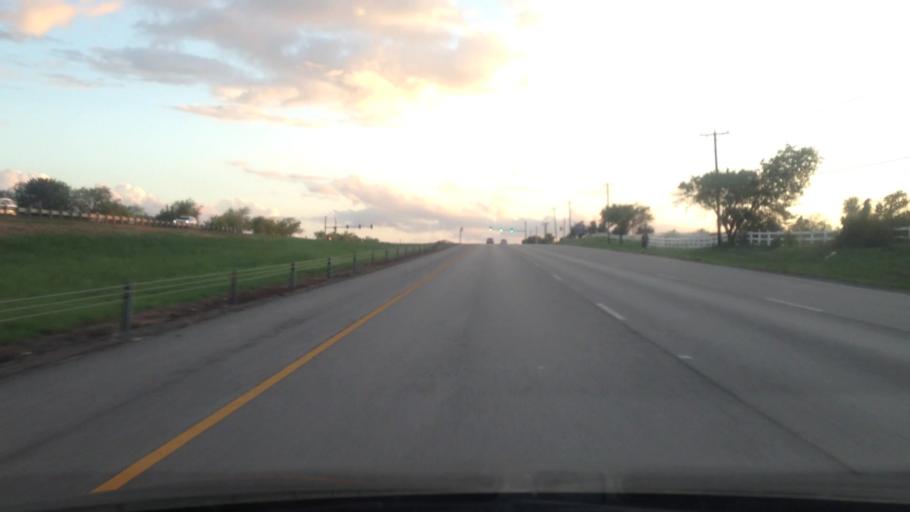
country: US
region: Texas
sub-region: Tarrant County
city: Benbrook
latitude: 32.6521
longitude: -97.4986
